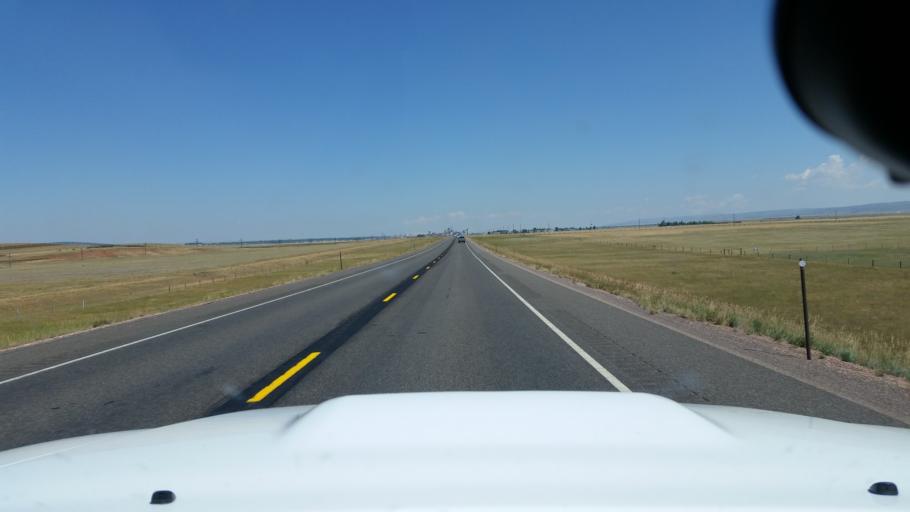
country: US
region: Wyoming
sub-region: Albany County
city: Laramie
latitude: 41.2286
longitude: -105.6005
